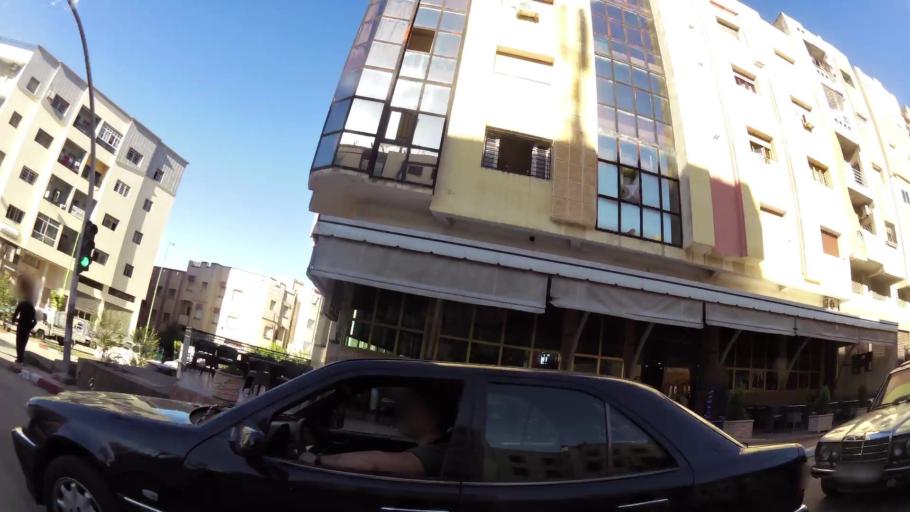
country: MA
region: Meknes-Tafilalet
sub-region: Meknes
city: Meknes
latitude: 33.8658
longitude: -5.5766
